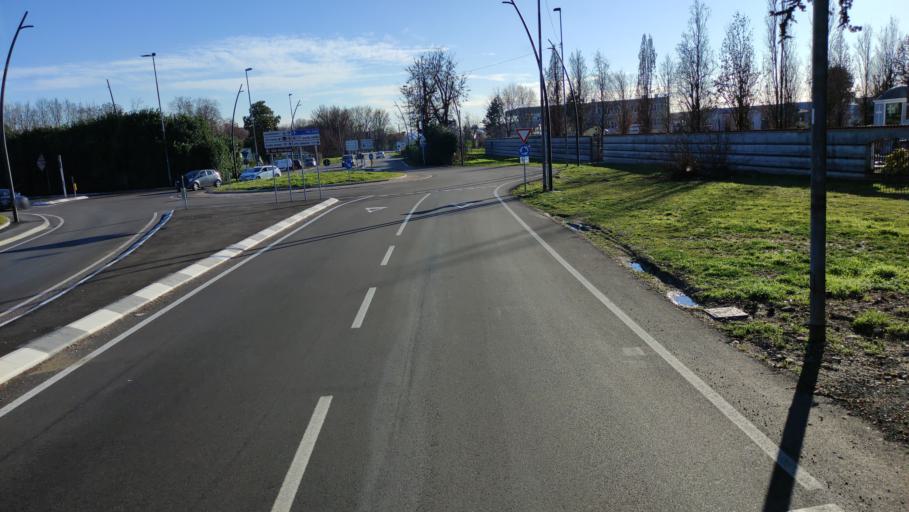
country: IT
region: Lombardy
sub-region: Provincia di Monza e Brianza
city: Concorezzo
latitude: 45.5875
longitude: 9.3305
